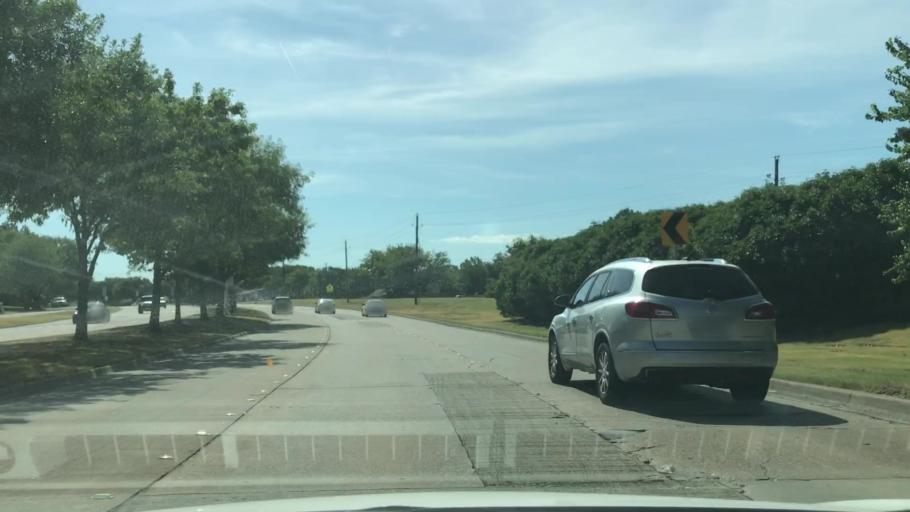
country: US
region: Texas
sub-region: Collin County
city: Plano
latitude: 33.0560
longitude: -96.7261
